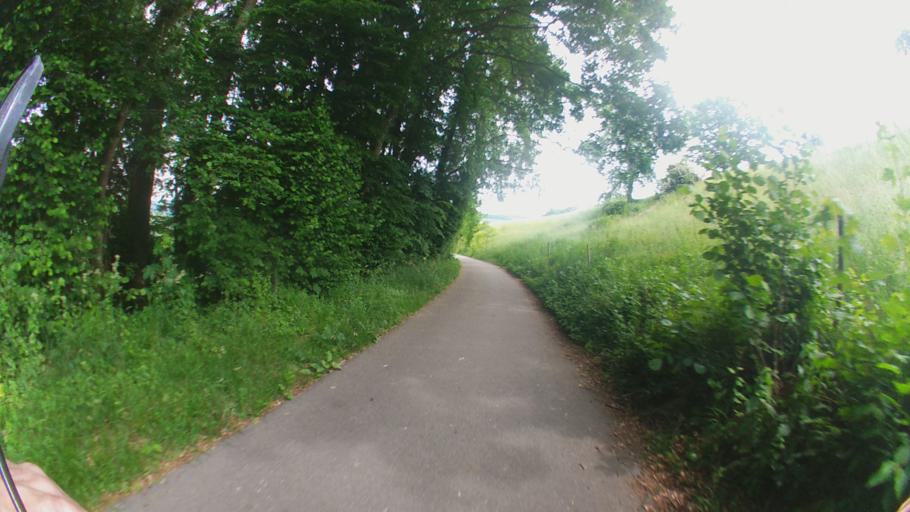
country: CH
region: Aargau
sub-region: Bezirk Baden
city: Unterehrendingen
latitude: 47.5116
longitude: 8.3288
